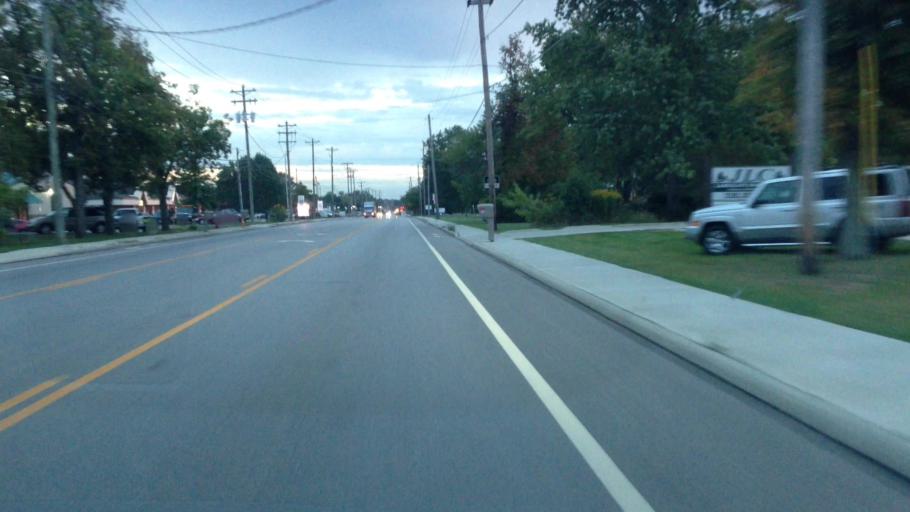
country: US
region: Ohio
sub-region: Summit County
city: Cuyahoga Falls
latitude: 41.1787
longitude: -81.5086
